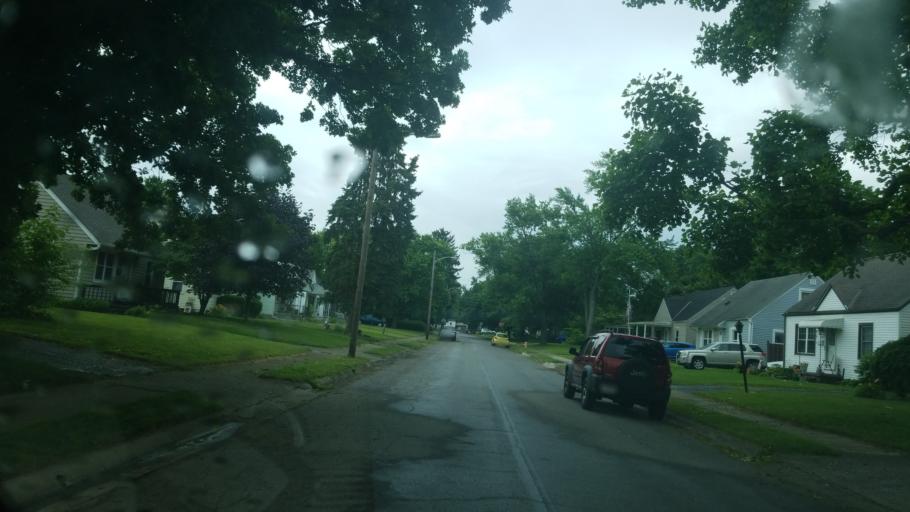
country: US
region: Ohio
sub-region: Franklin County
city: Columbus
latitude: 40.0276
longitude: -82.9928
